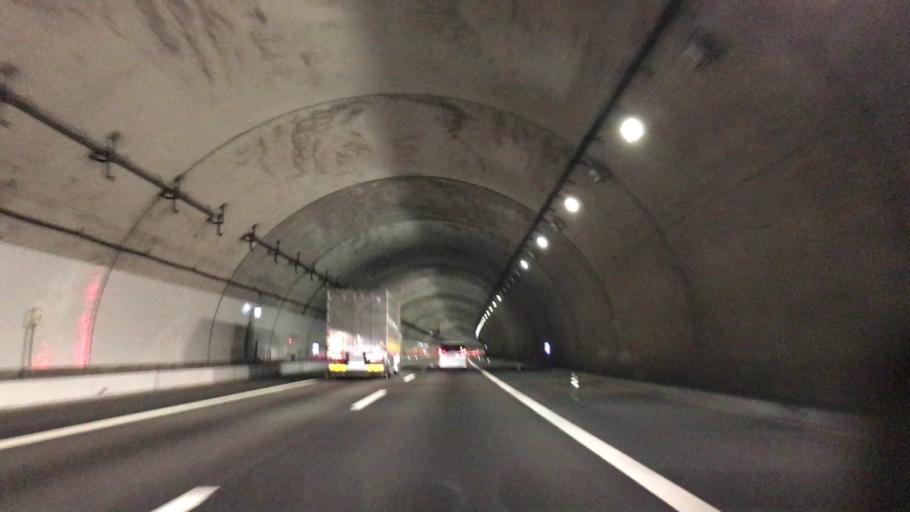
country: JP
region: Shiga Prefecture
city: Minakuchicho-matoba
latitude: 34.9234
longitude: 136.1130
